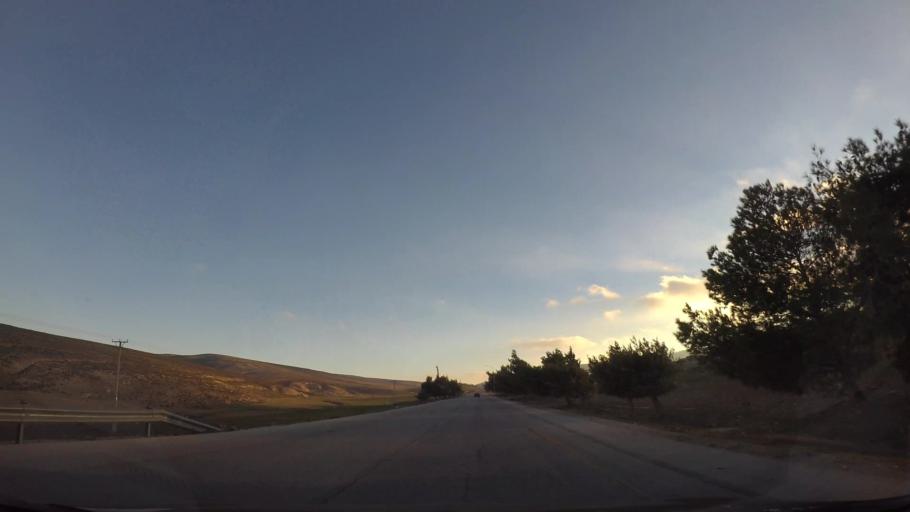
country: JO
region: Ma'an
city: Petra
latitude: 30.4493
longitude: 35.5246
